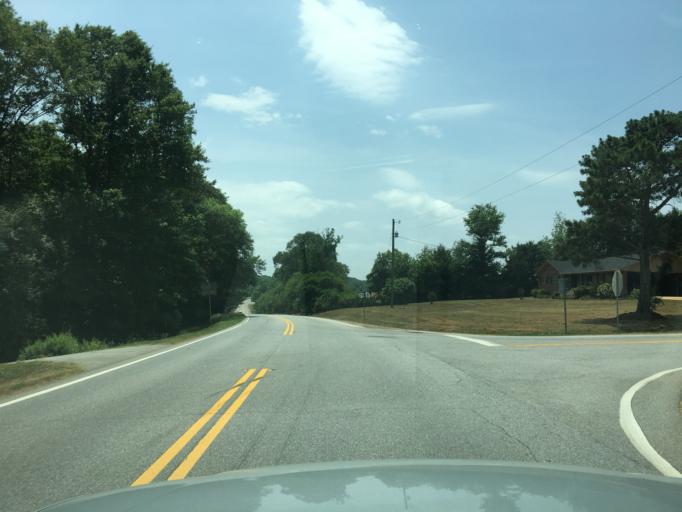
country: US
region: Georgia
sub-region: Hart County
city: Royston
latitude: 34.2434
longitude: -83.1767
